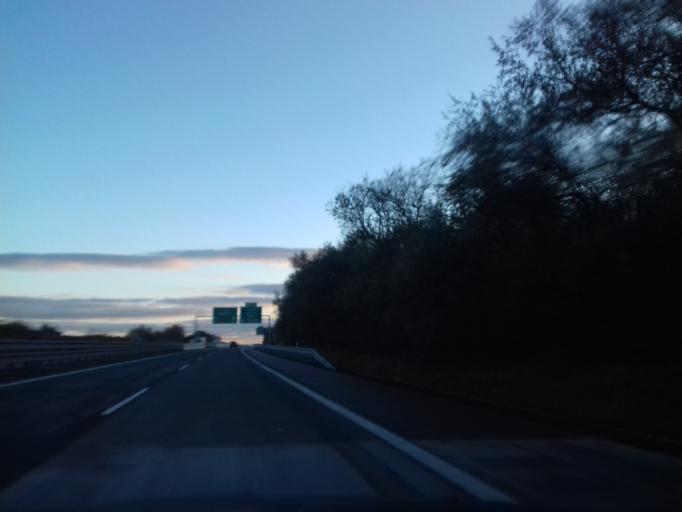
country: CZ
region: South Moravian
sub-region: Okres Vyskov
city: Vyskov
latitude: 49.2682
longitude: 17.0097
